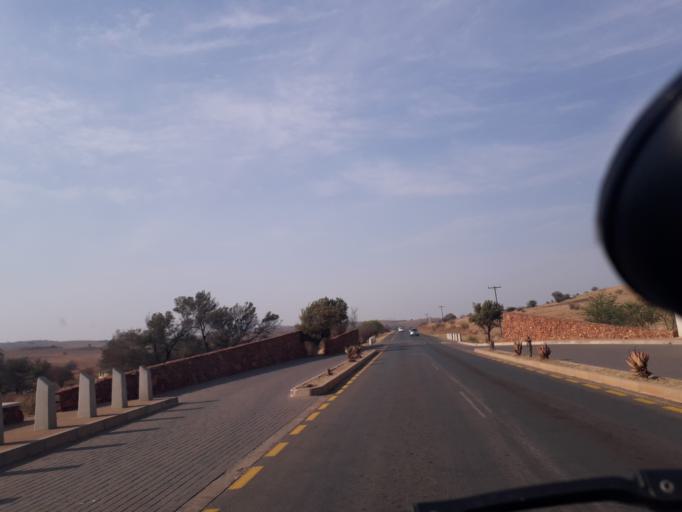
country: ZA
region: Gauteng
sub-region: West Rand District Municipality
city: Krugersdorp
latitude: -26.0217
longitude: 27.7247
